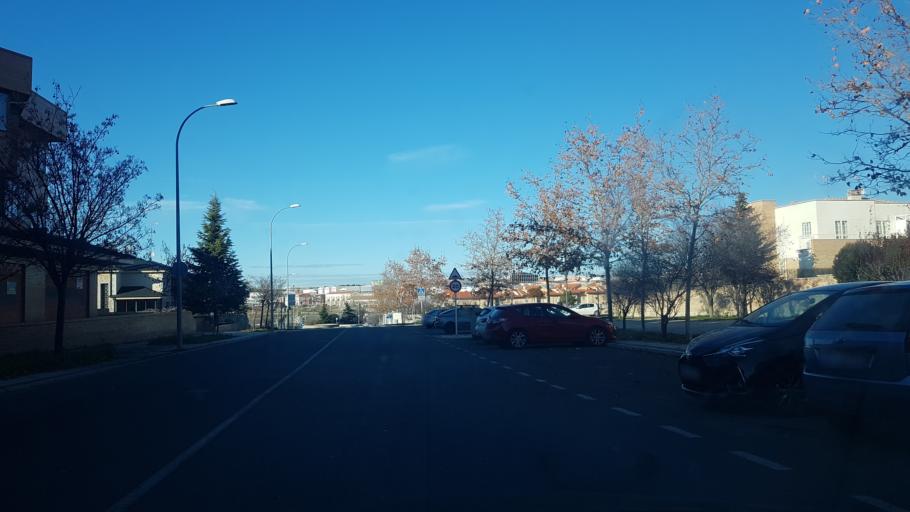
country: ES
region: Castille and Leon
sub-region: Provincia de Avila
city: Avila
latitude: 40.6581
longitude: -4.6785
